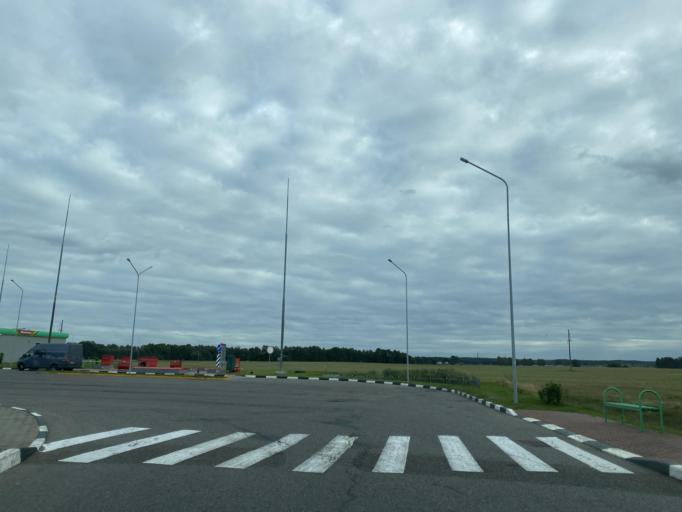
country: BY
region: Grodnenskaya
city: Smarhon'
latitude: 54.4570
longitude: 26.3861
